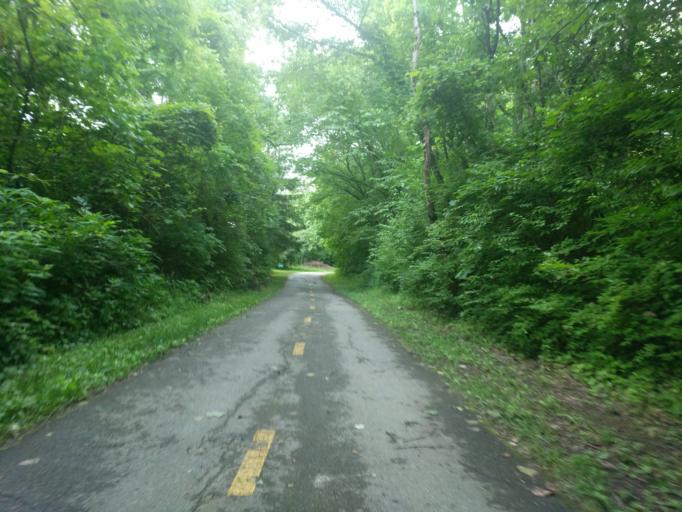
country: US
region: Ohio
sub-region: Franklin County
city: Minerva Park
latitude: 40.0621
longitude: -82.9246
